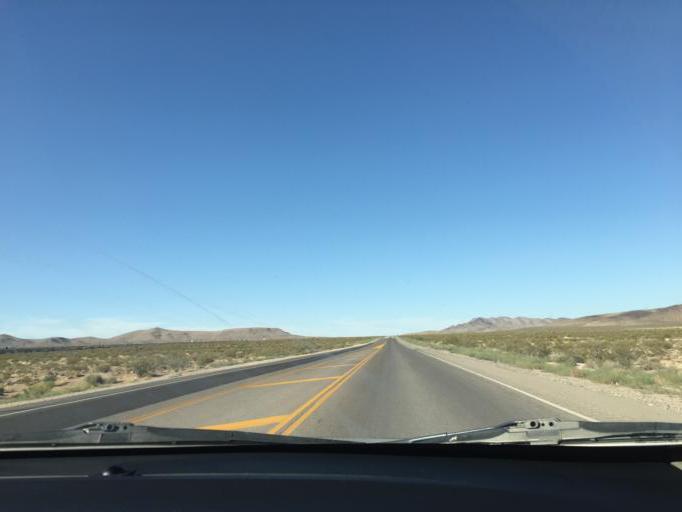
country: US
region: Nevada
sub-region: Clark County
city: Enterprise
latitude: 35.8415
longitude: -115.2698
